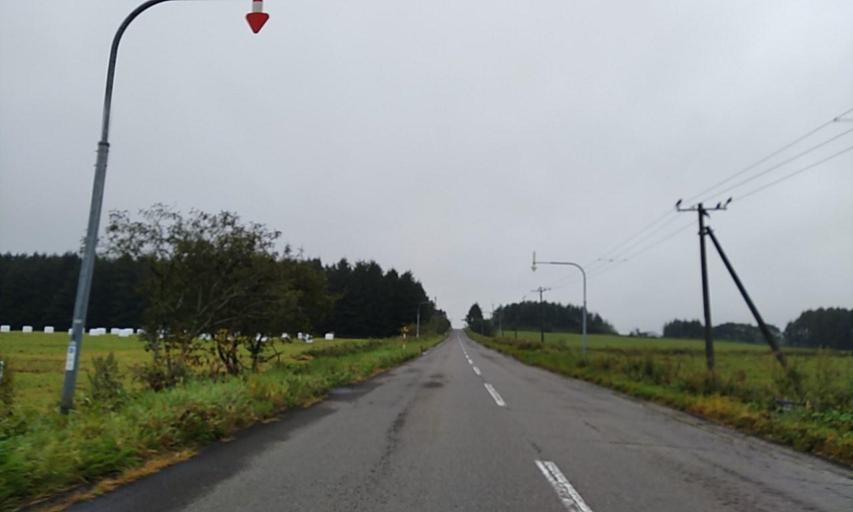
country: JP
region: Hokkaido
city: Shibetsu
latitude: 43.5088
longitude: 144.6674
